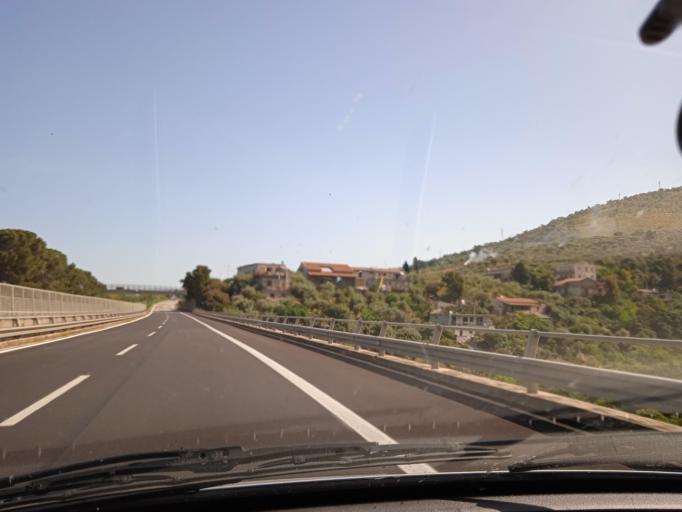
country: IT
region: Sicily
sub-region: Messina
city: Rocca di Capri Leone
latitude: 38.1169
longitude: 14.7262
